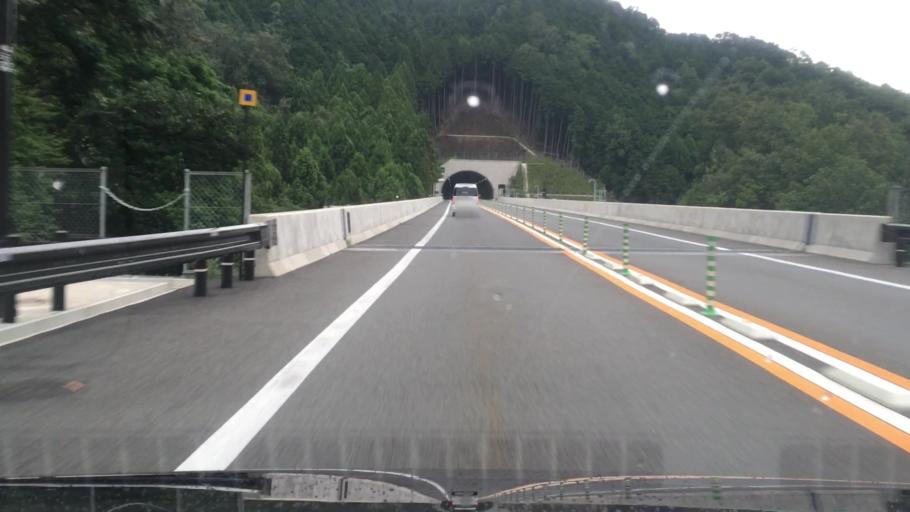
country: JP
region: Hyogo
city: Toyooka
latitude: 35.4412
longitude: 134.7674
